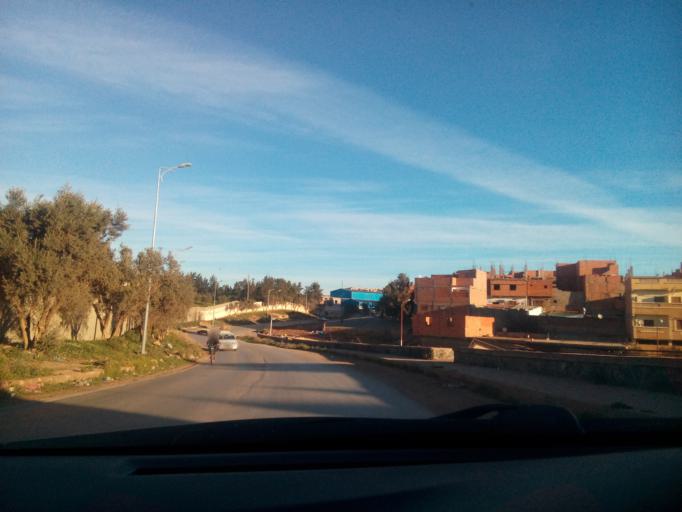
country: DZ
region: Oran
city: Es Senia
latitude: 35.6367
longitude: -0.6742
